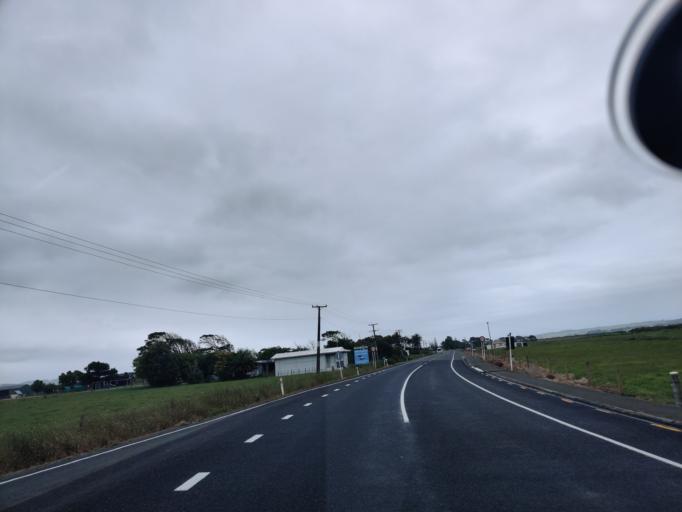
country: NZ
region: Northland
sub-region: Kaipara District
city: Dargaville
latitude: -36.1227
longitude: 174.0146
